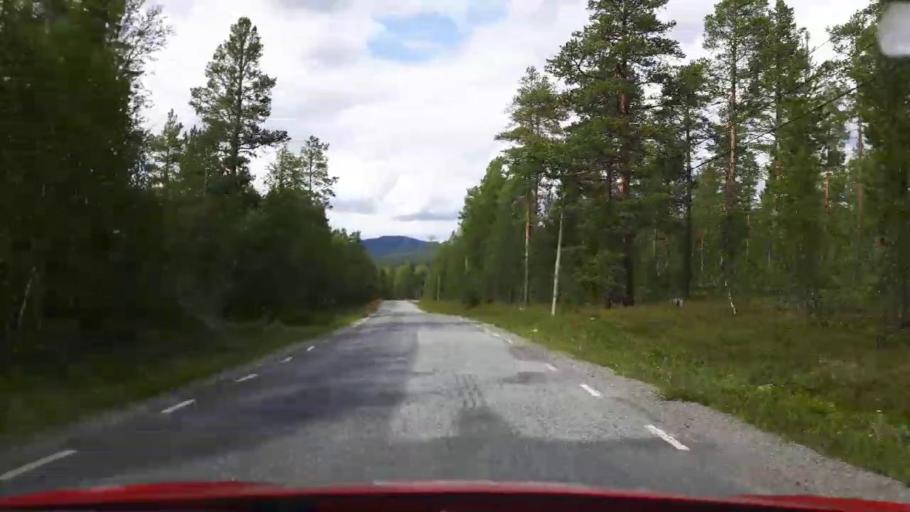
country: NO
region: Hedmark
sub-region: Engerdal
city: Engerdal
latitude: 62.4221
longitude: 12.6911
